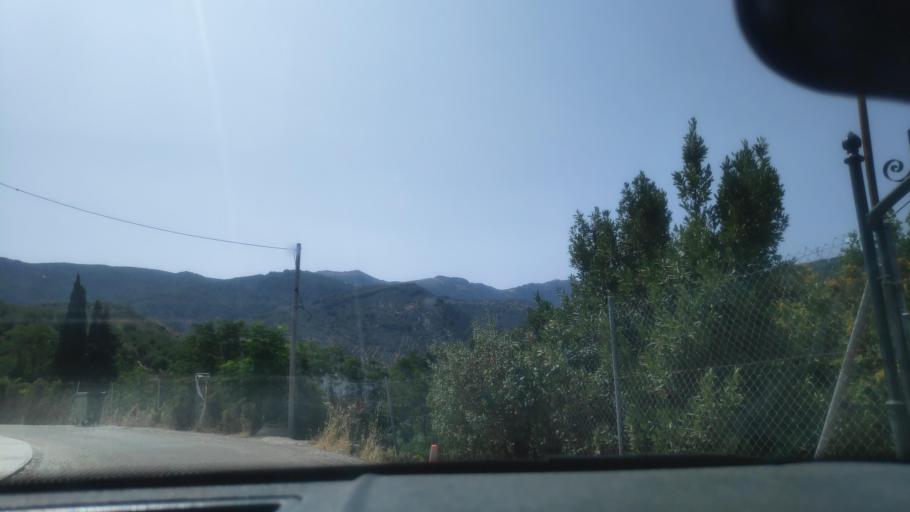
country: ES
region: Andalusia
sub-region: Provincia de Jaen
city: Jodar
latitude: 37.8004
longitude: -3.4123
